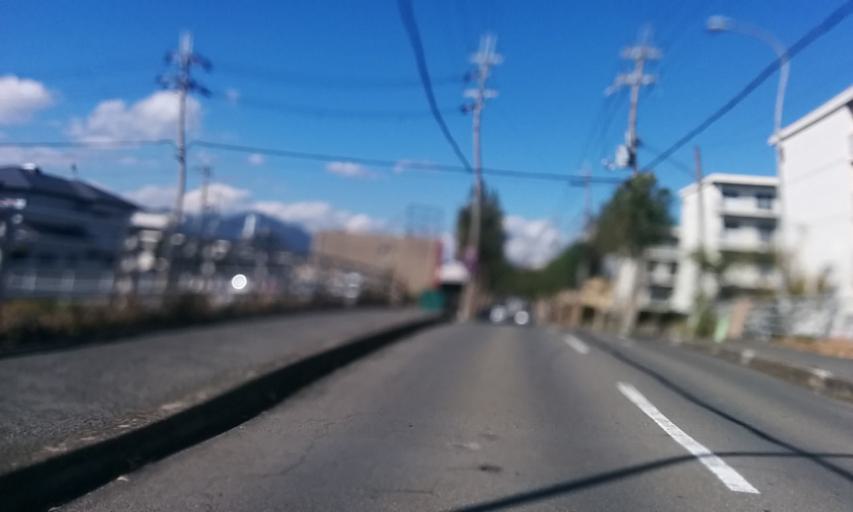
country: JP
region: Kyoto
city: Kameoka
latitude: 35.0192
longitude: 135.5746
